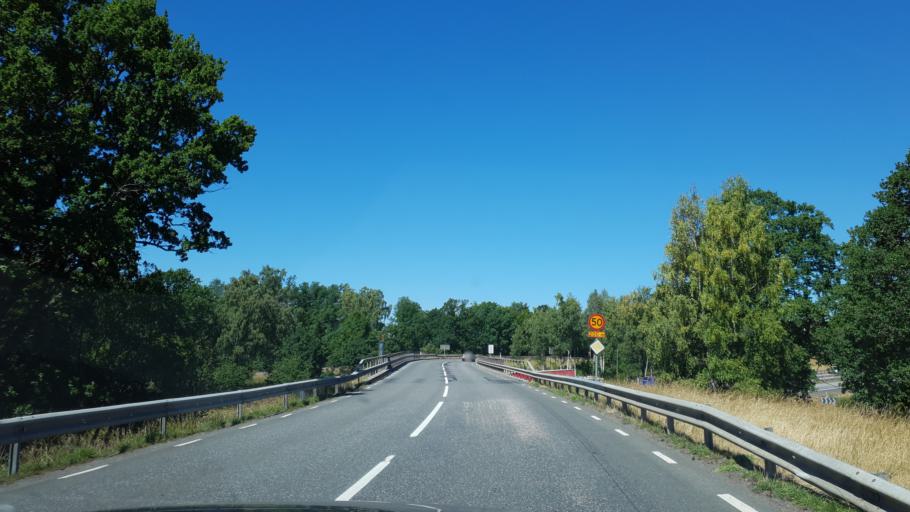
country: SE
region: Joenkoeping
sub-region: Jonkopings Kommun
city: Graenna
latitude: 57.9925
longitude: 14.4394
